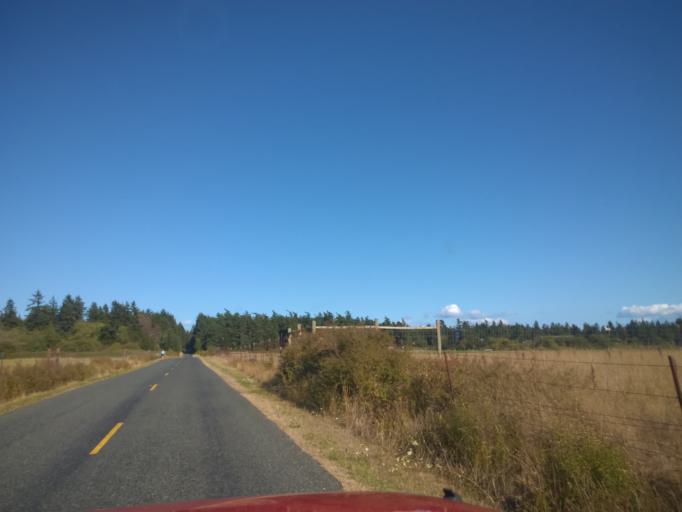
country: US
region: Washington
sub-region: San Juan County
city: Friday Harbor
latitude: 48.5323
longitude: -122.8739
